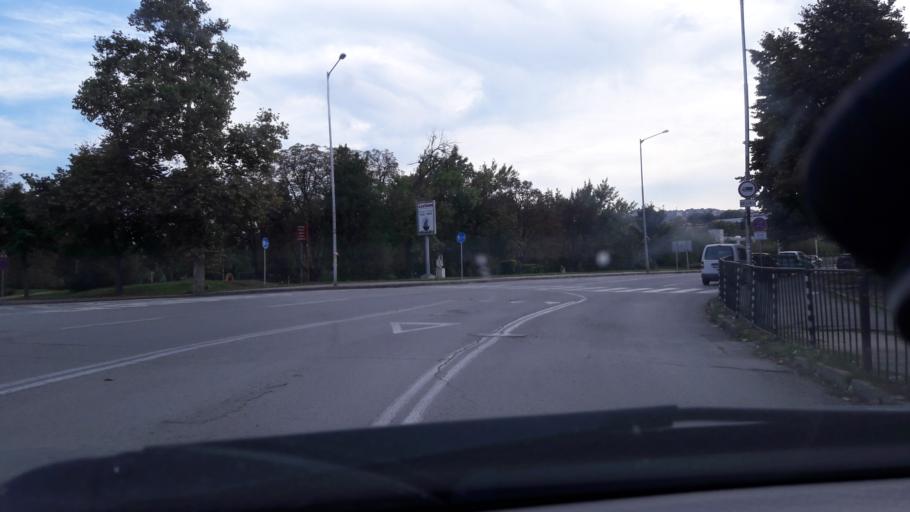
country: BG
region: Razgrad
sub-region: Obshtina Razgrad
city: Razgrad
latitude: 43.5295
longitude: 26.5201
